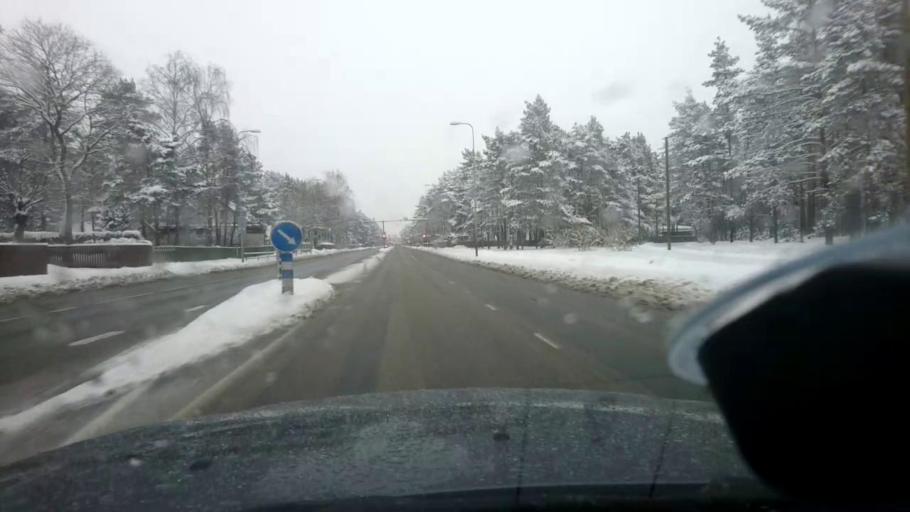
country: EE
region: Harju
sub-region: Tallinna linn
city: Tallinn
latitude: 59.3839
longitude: 24.7075
